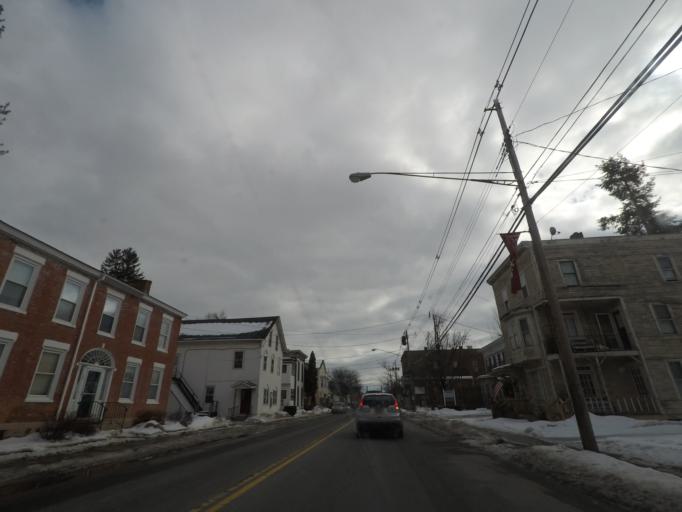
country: US
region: New York
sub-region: Washington County
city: Greenwich
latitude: 43.0911
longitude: -73.5007
